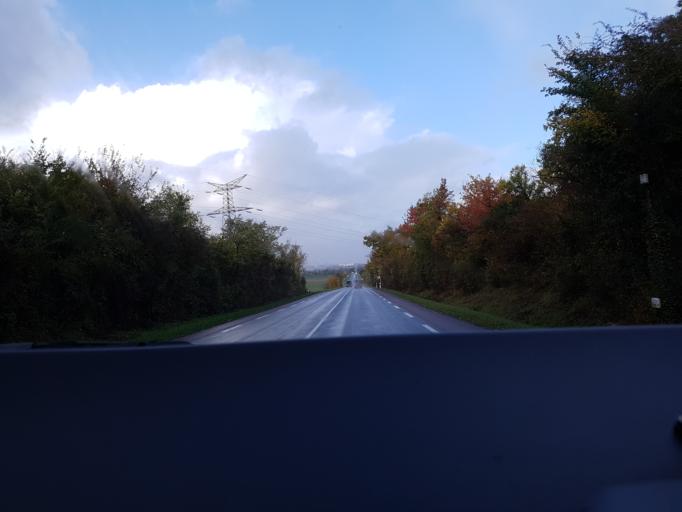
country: FR
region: Poitou-Charentes
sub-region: Departement de la Charente-Maritime
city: Les Gonds
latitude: 45.6789
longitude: -0.6066
